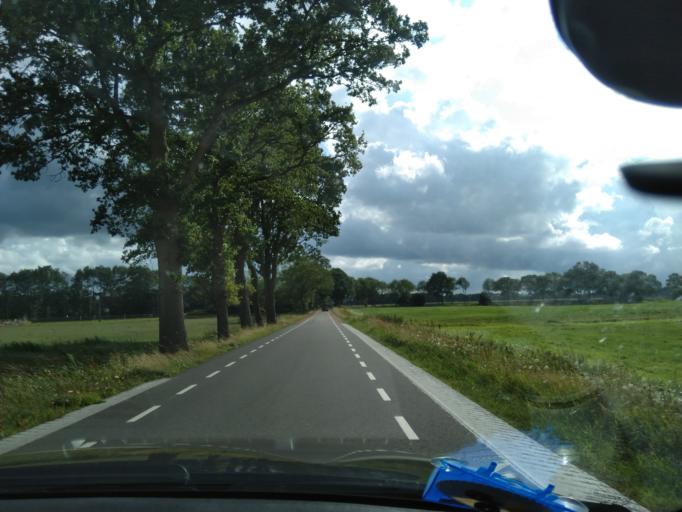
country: NL
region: Drenthe
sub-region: Gemeente Assen
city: Assen
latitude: 53.0380
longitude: 6.5382
